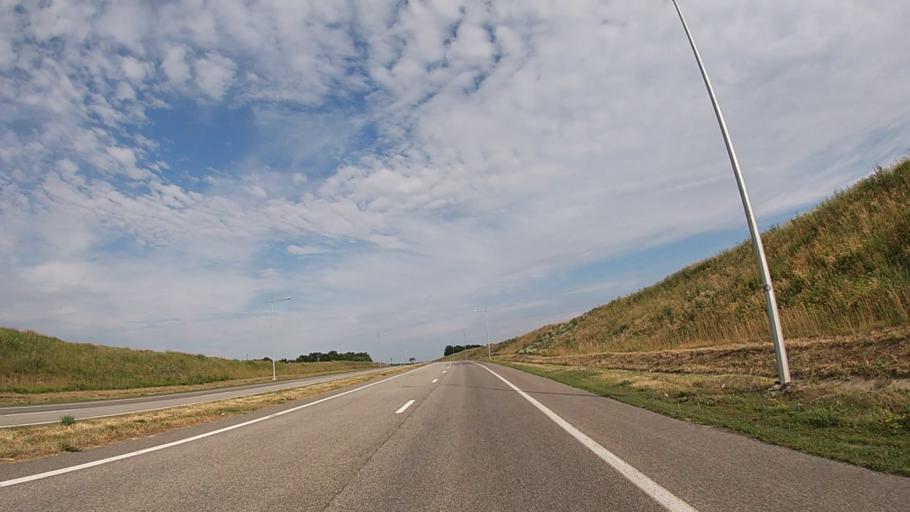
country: RU
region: Belgorod
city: Tomarovka
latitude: 50.7052
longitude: 36.2184
